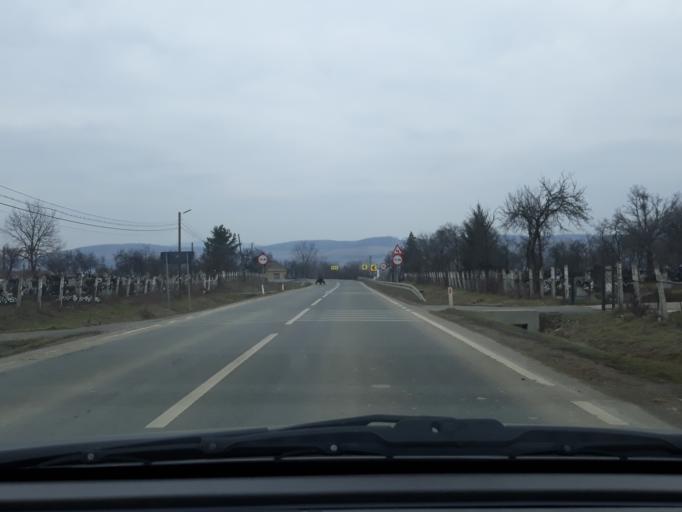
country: RO
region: Salaj
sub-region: Comuna Nusfalau
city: Nusfalau
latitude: 47.1884
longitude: 22.6993
